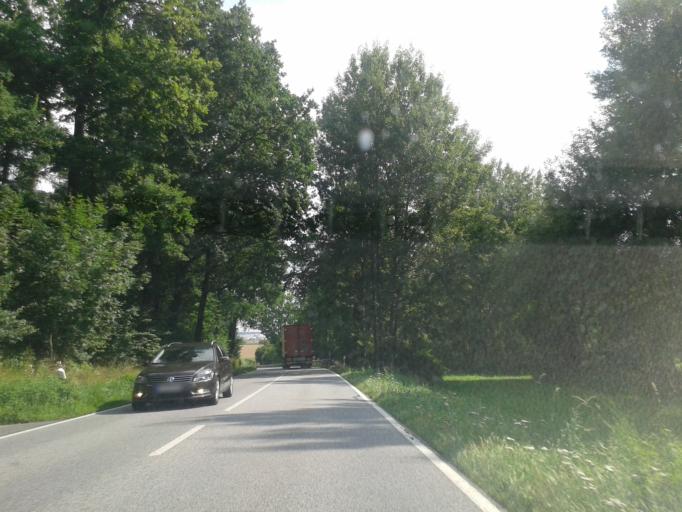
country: DE
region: Saxony
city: Radeberg
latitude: 51.1350
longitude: 13.9466
